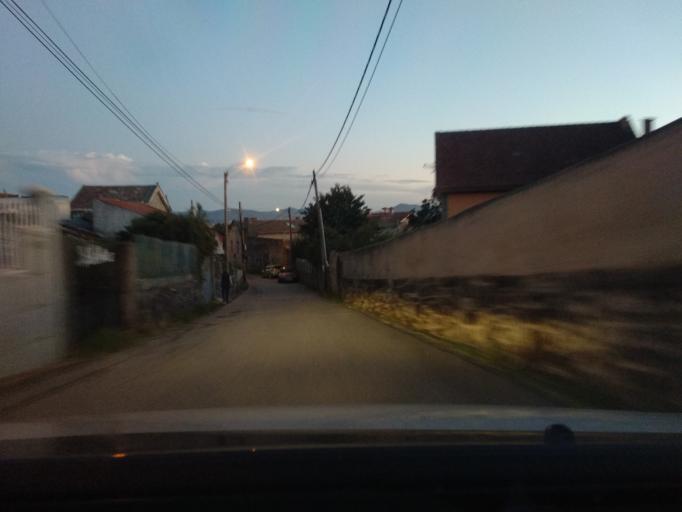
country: ES
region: Galicia
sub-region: Provincia de Pontevedra
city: Moana
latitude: 42.2826
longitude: -8.7469
